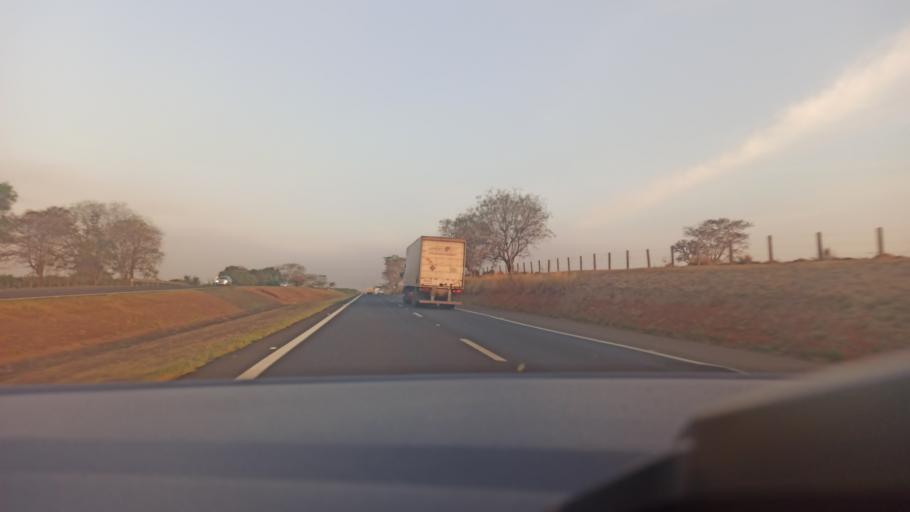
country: BR
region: Sao Paulo
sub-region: Taquaritinga
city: Taquaritinga
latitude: -21.4418
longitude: -48.6476
